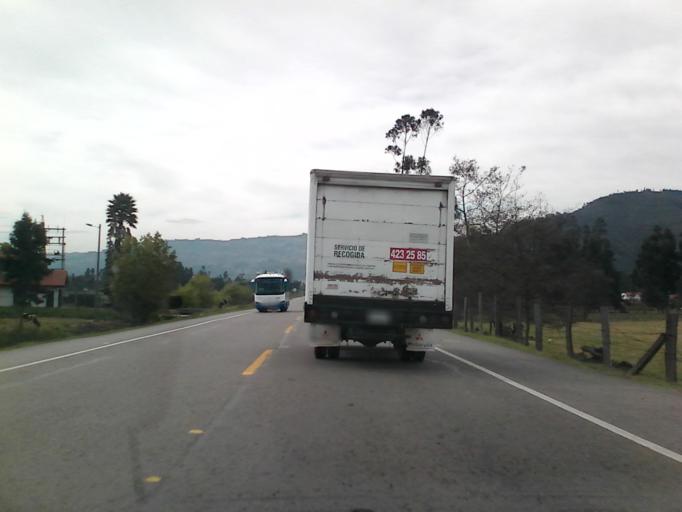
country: CO
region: Boyaca
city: Tibasosa
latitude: 5.7805
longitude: -72.9966
